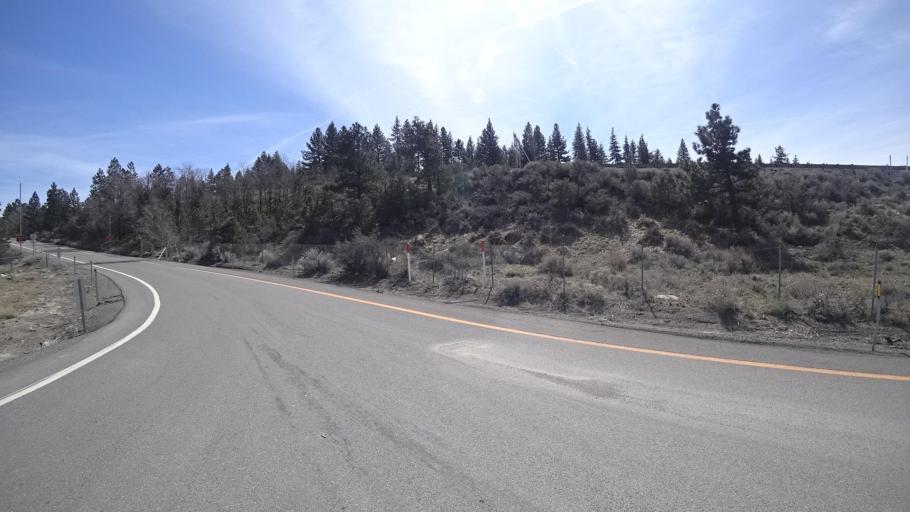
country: US
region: Nevada
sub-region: Washoe County
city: Verdi
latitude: 39.5126
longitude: -119.9922
